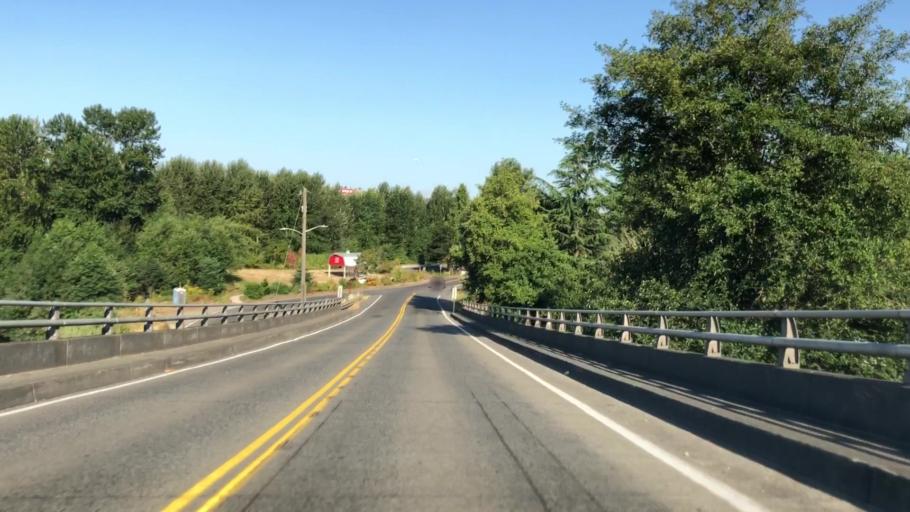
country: US
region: Washington
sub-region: King County
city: Tukwila
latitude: 47.4896
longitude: -122.2669
